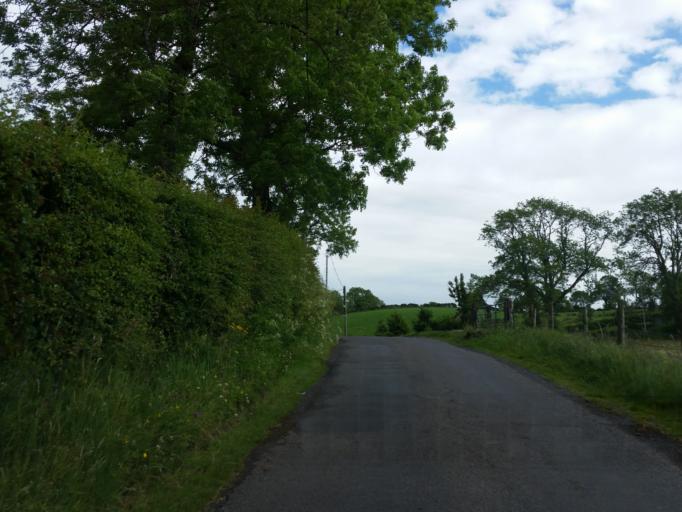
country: GB
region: Northern Ireland
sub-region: Omagh District
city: Omagh
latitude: 54.5470
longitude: -7.1288
